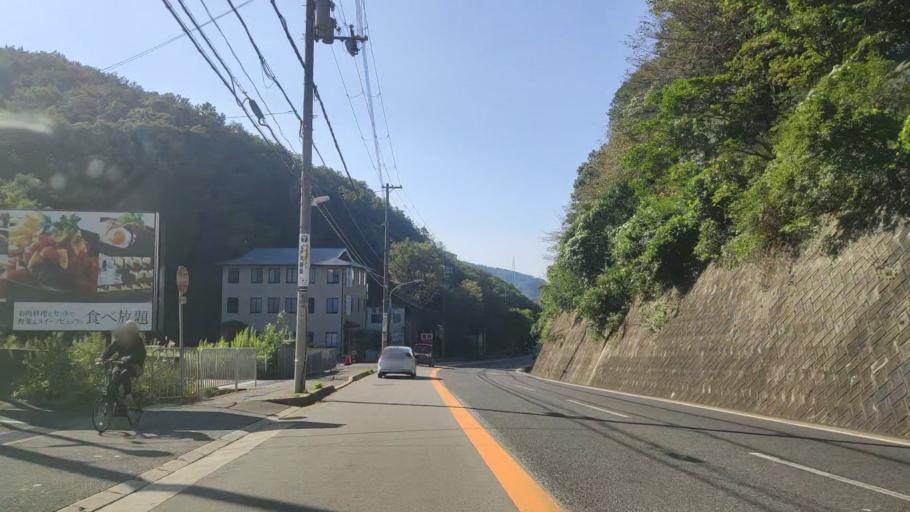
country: JP
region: Hyogo
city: Kobe
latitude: 34.7348
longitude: 135.1588
